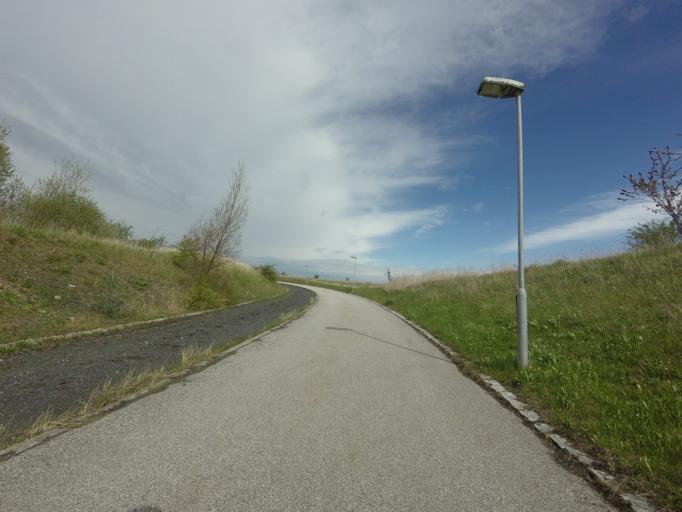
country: SE
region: Skane
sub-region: Malmo
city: Bunkeflostrand
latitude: 55.5480
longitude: 12.9698
